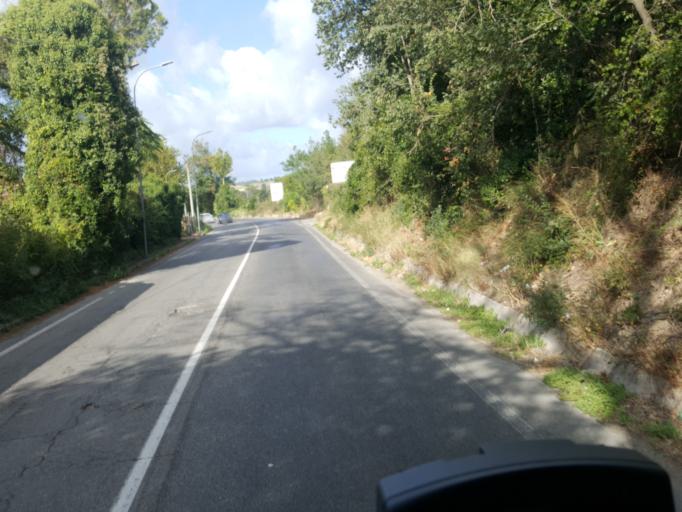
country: IT
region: Latium
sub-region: Citta metropolitana di Roma Capitale
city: Girardi-Bellavista-Terrazze
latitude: 42.0956
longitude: 12.5715
